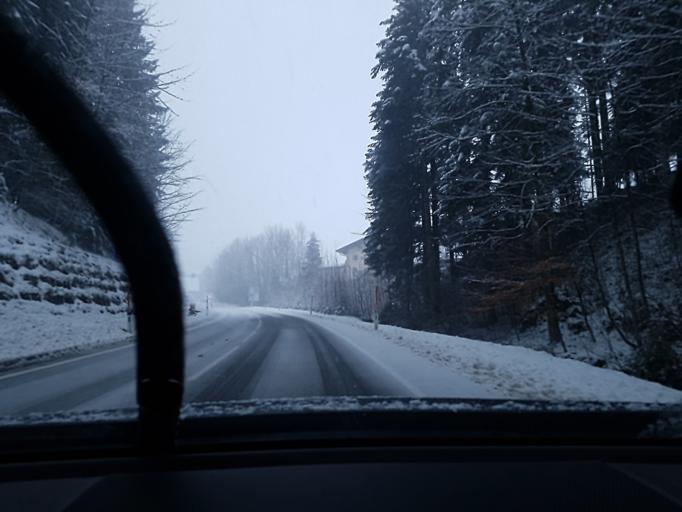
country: AT
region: Salzburg
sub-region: Politischer Bezirk Hallein
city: Abtenau
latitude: 47.5644
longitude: 13.3798
